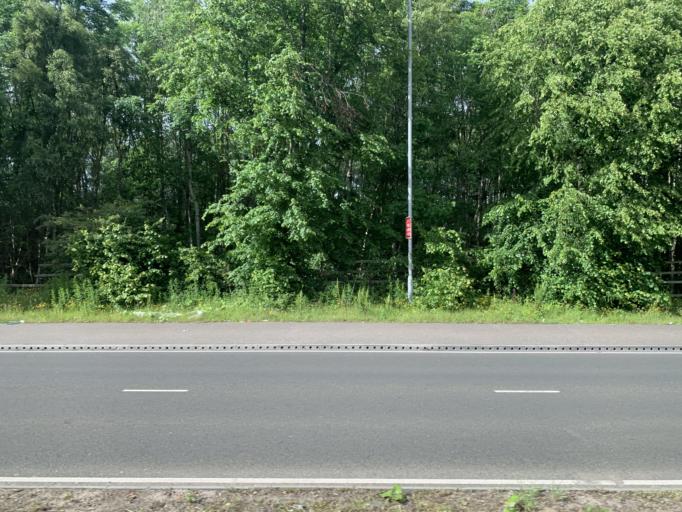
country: GB
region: Scotland
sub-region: South Lanarkshire
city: Uddingston
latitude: 55.8525
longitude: -4.1016
